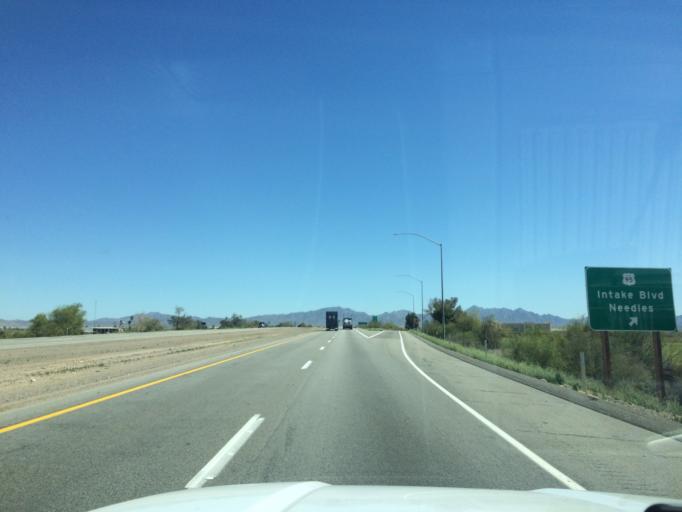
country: US
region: California
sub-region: Riverside County
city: Blythe
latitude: 33.6072
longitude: -114.5753
